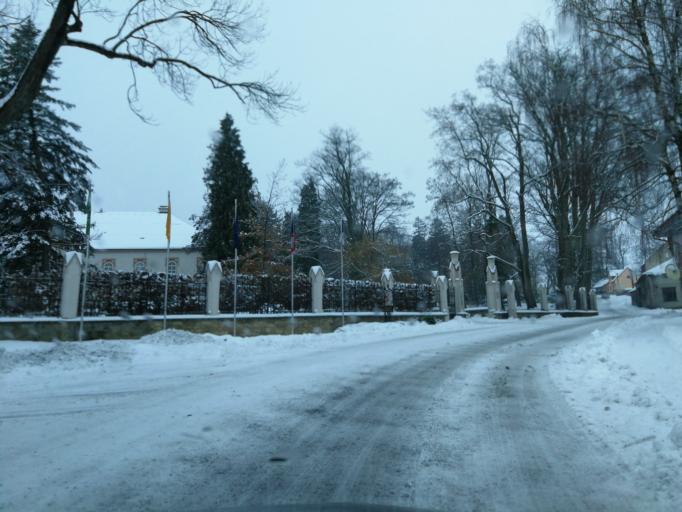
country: CZ
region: Vysocina
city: Heralec
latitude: 49.5308
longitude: 15.4559
